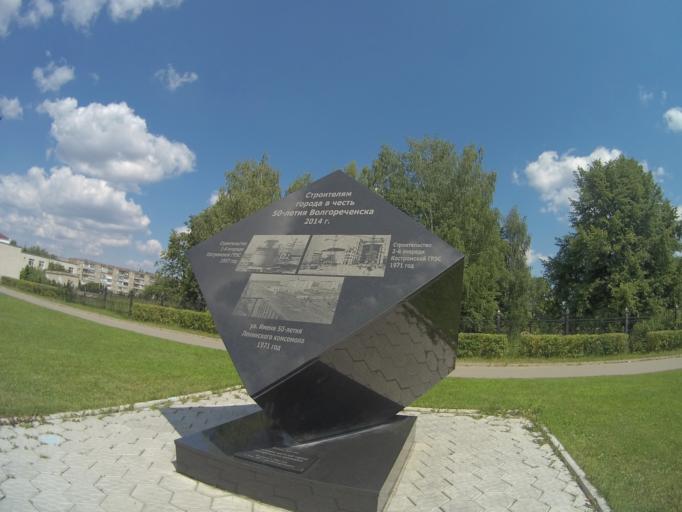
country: RU
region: Kostroma
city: Volgorechensk
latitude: 57.4412
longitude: 41.1552
